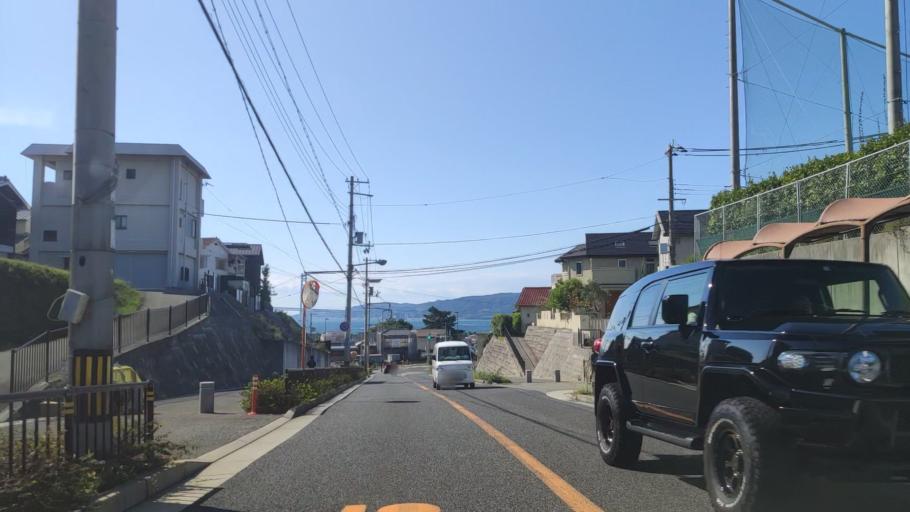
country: JP
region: Hyogo
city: Akashi
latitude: 34.6498
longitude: 135.0058
